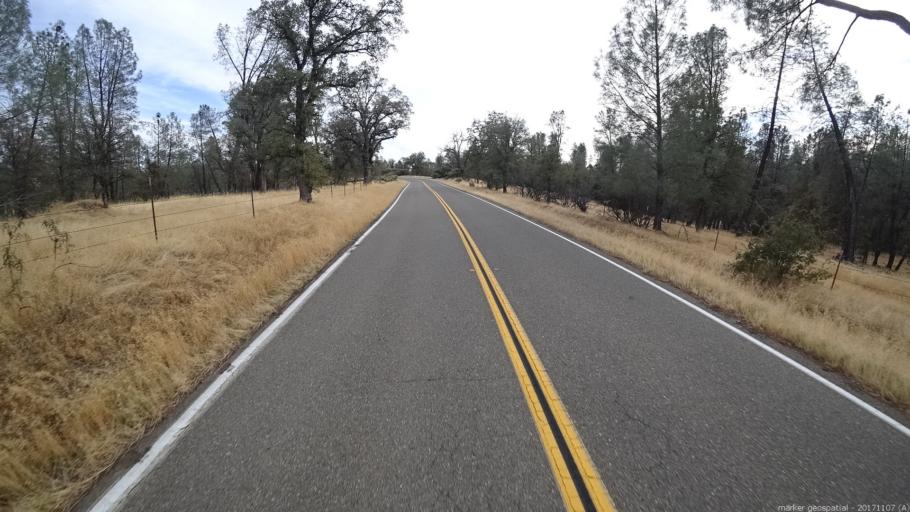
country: US
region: California
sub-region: Shasta County
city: Shasta
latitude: 40.5016
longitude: -122.5280
